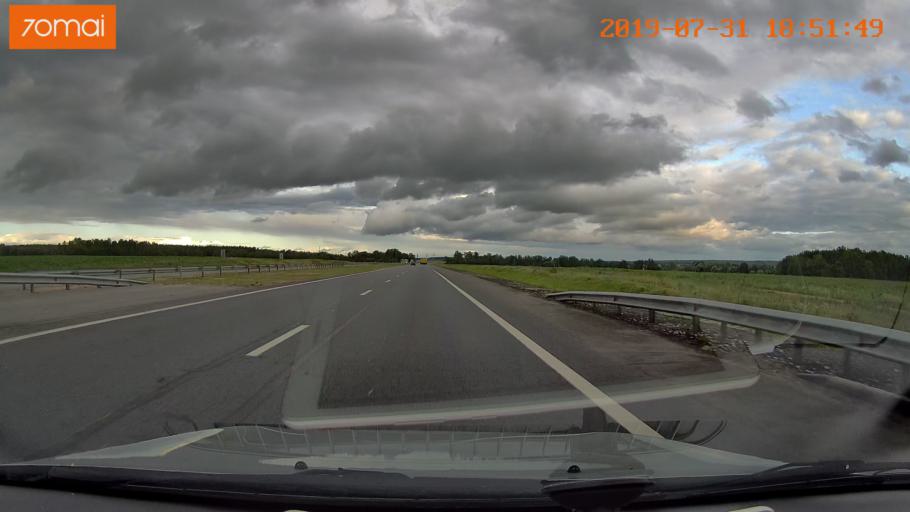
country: RU
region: Moskovskaya
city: Voskresensk
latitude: 55.2190
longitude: 38.6164
